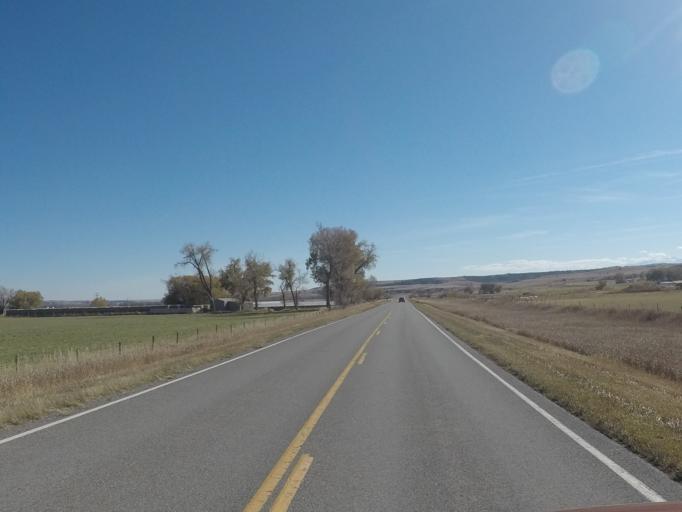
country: US
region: Montana
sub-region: Sweet Grass County
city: Big Timber
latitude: 45.8061
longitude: -109.8675
